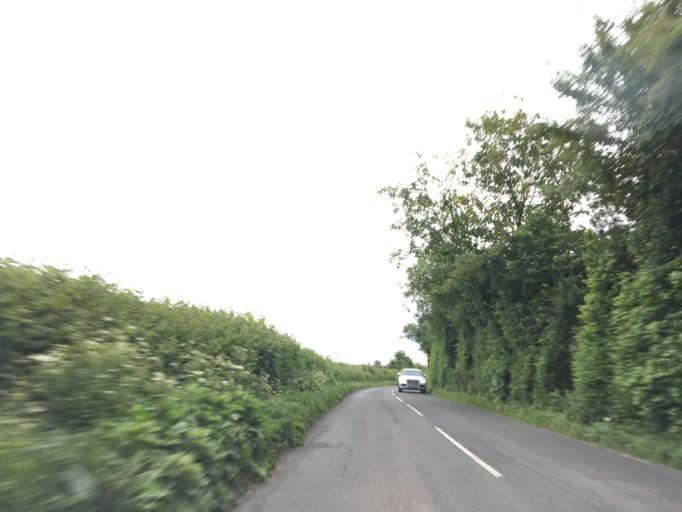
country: GB
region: England
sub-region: Gloucestershire
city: Stonehouse
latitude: 51.7798
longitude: -2.3429
